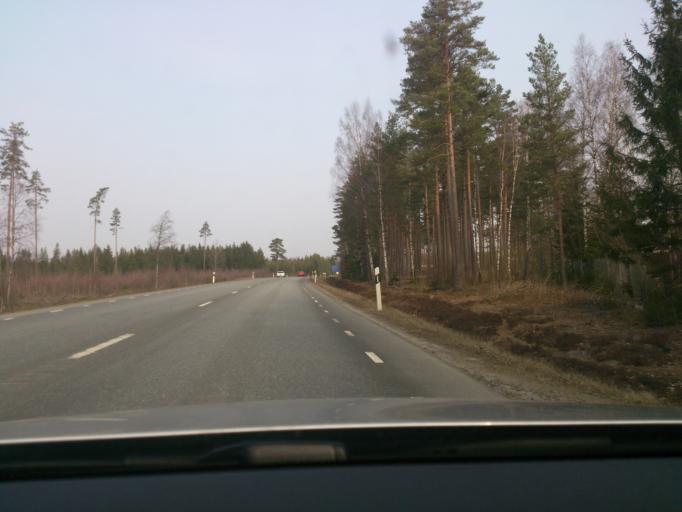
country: SE
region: Kronoberg
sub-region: Alvesta Kommun
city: Moheda
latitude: 56.9941
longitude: 14.5603
